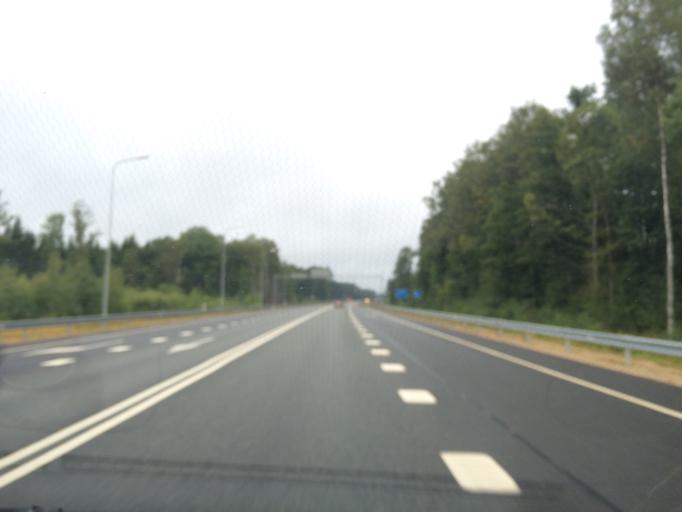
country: LV
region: Kegums
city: Kegums
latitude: 56.8254
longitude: 24.7556
